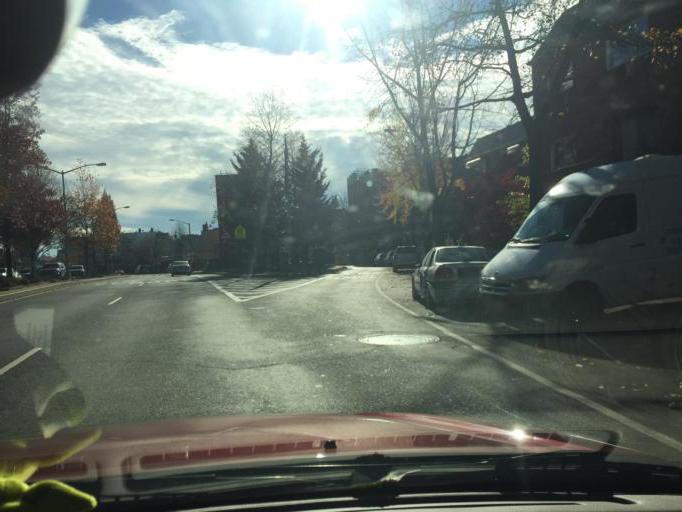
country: US
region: New York
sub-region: Queens County
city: Long Island City
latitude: 40.7236
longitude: -73.9476
